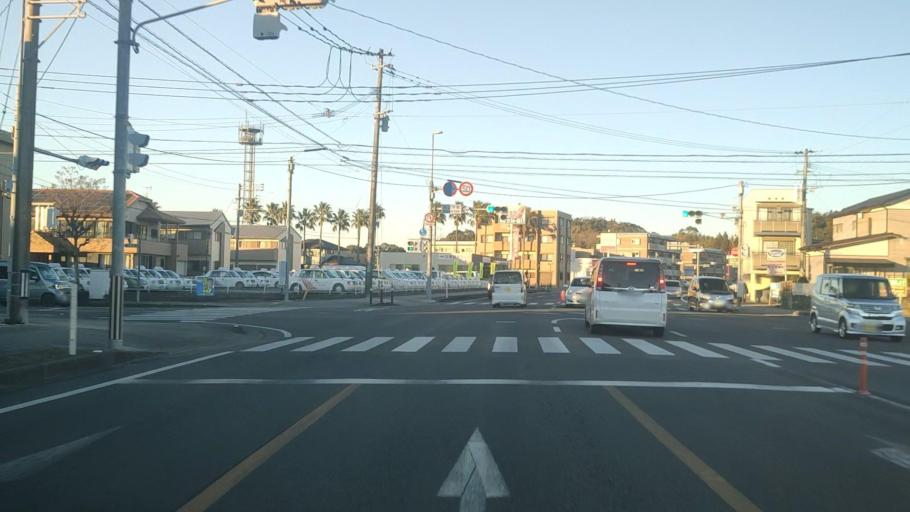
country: JP
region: Miyazaki
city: Miyazaki-shi
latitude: 31.9012
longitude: 131.4057
